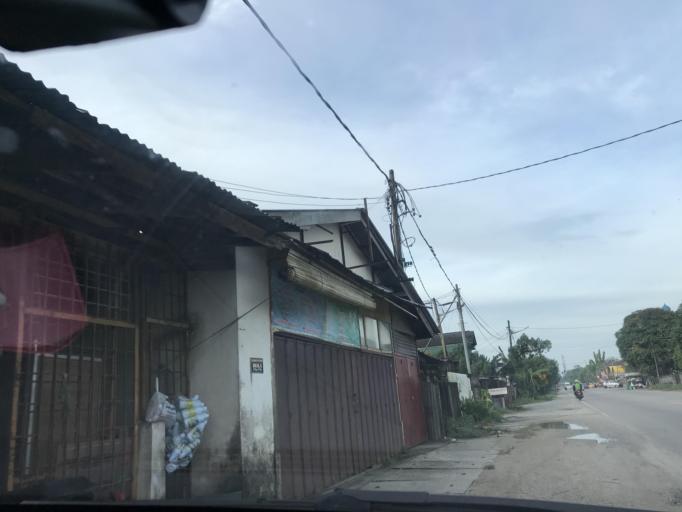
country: MY
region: Kelantan
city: Kota Bharu
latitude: 6.1018
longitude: 102.2107
